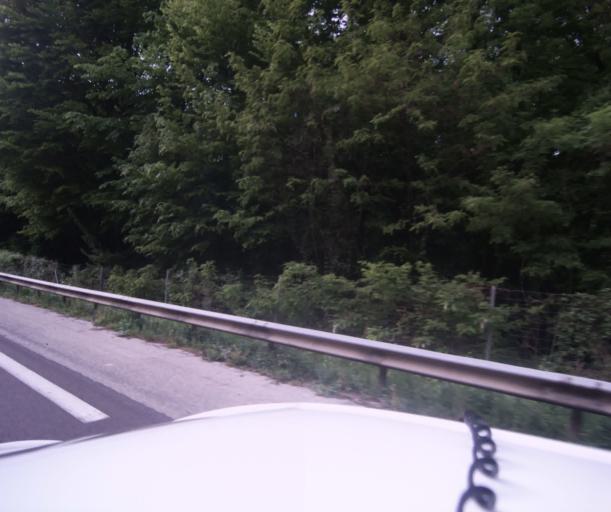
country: FR
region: Franche-Comte
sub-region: Departement du Doubs
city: Franois
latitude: 47.2131
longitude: 5.9290
